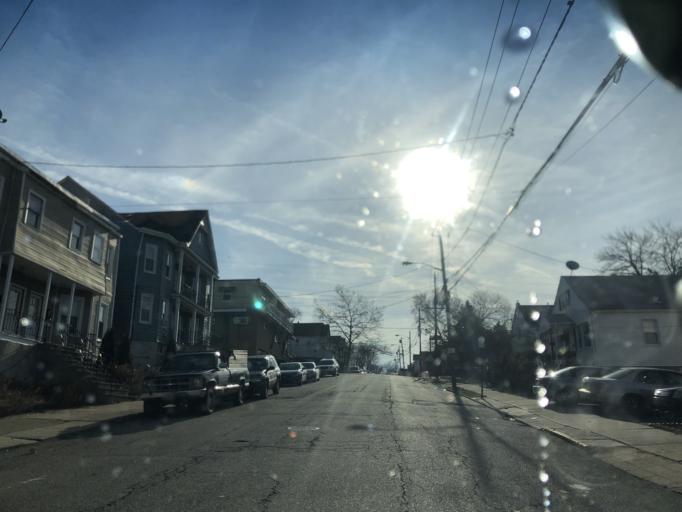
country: US
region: New Jersey
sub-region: Passaic County
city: Hawthorne
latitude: 40.9362
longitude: -74.1463
